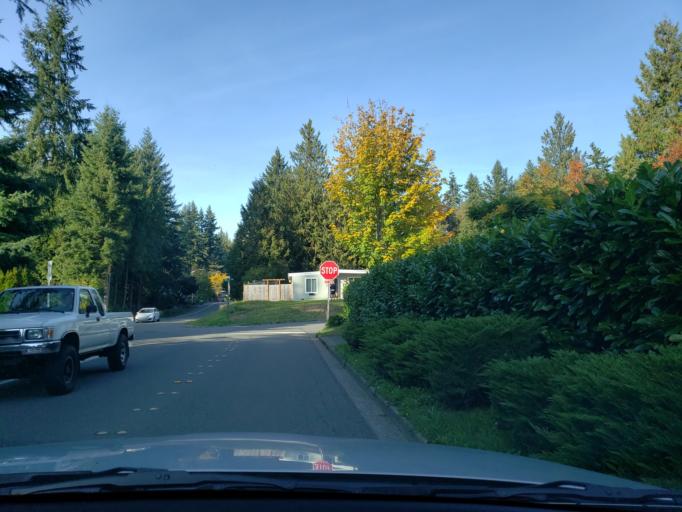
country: US
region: Washington
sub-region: Snohomish County
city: Meadowdale
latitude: 47.8667
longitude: -122.3144
